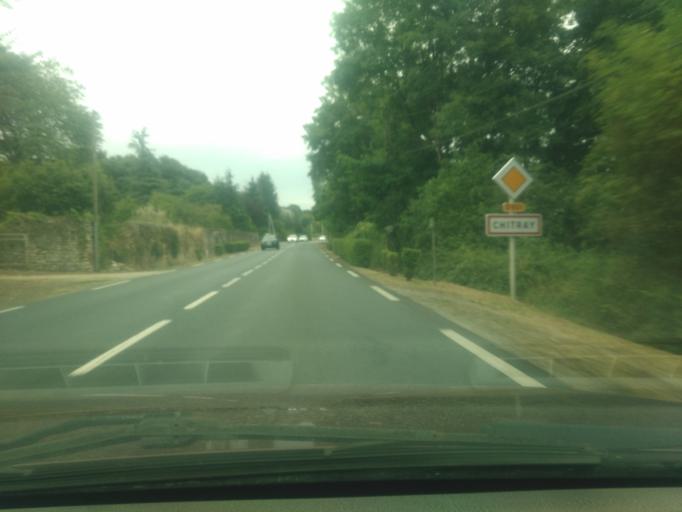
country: FR
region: Centre
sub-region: Departement de l'Indre
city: Saint-Gaultier
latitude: 46.6366
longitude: 1.3551
